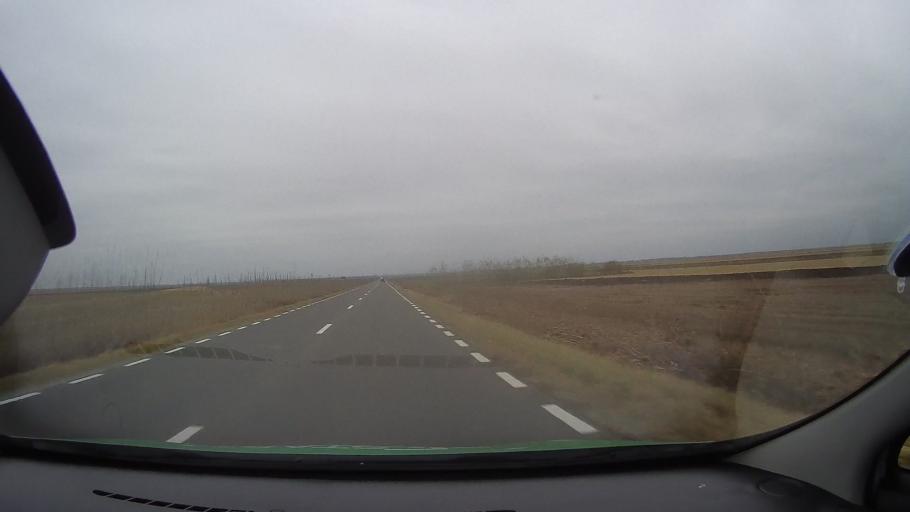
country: RO
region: Ialomita
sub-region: Comuna Gheorghe Lazar
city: Gheorghe Lazar
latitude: 44.6475
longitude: 27.4056
